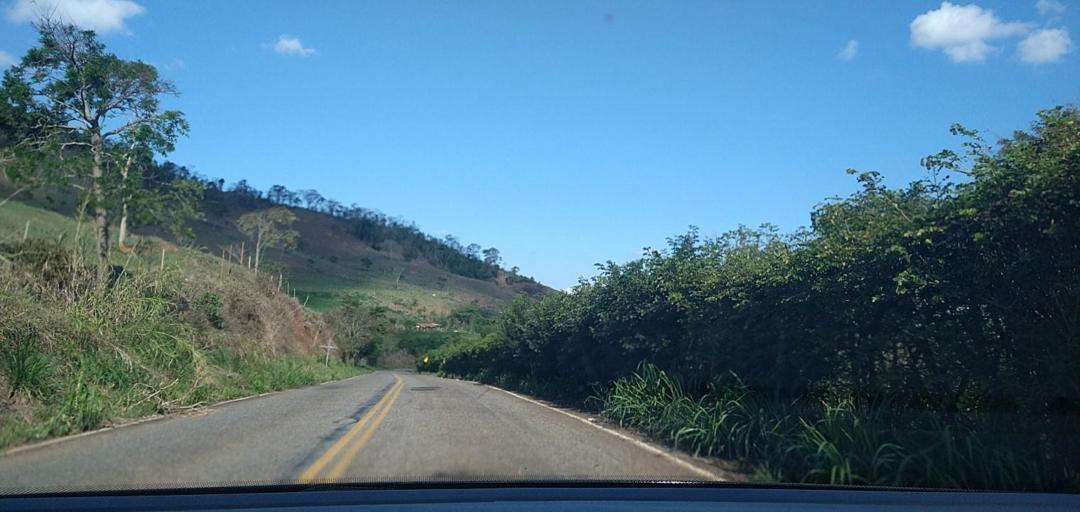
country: BR
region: Minas Gerais
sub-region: Alvinopolis
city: Alvinopolis
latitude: -20.1942
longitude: -42.9345
